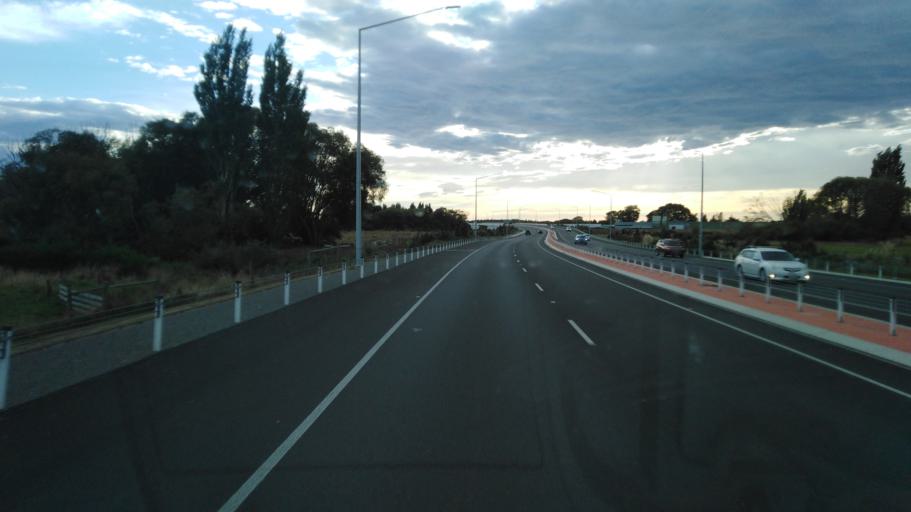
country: NZ
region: Canterbury
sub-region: Waimakariri District
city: Kaiapoi
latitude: -43.4378
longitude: 172.6271
